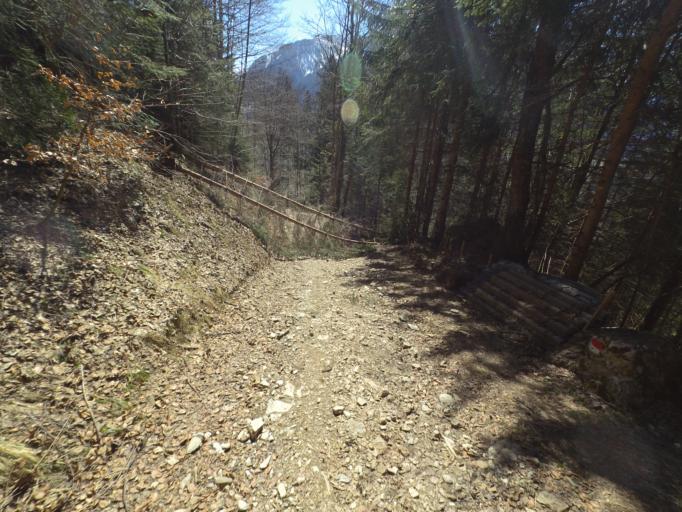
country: AT
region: Salzburg
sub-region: Politischer Bezirk Sankt Johann im Pongau
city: Sankt Veit im Pongau
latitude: 47.3360
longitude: 13.1594
